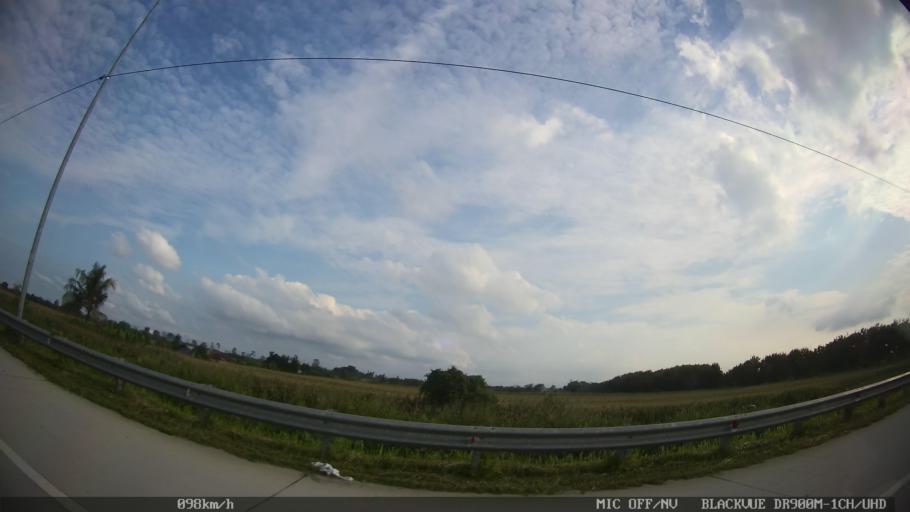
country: ID
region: North Sumatra
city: Medan
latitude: 3.6377
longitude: 98.6407
